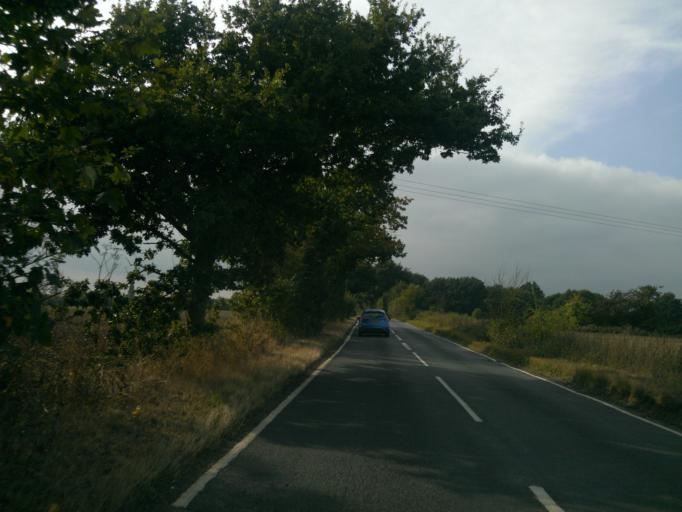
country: GB
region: England
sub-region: Essex
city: Great Totham
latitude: 51.7990
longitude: 0.7109
